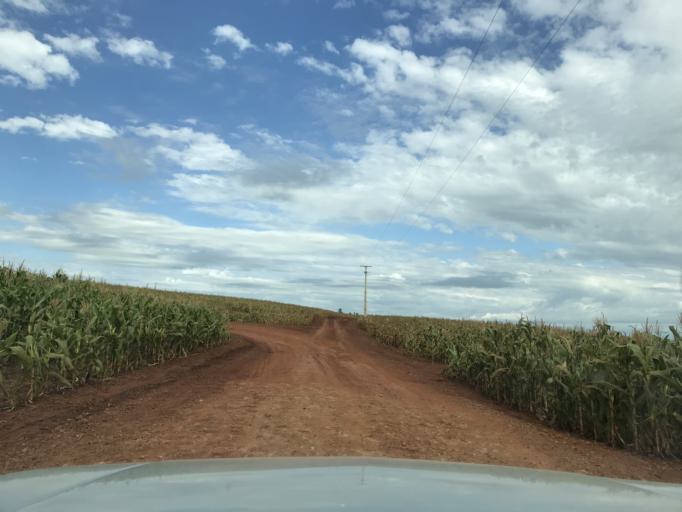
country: BR
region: Parana
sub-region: Palotina
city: Palotina
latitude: -24.3268
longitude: -53.8044
